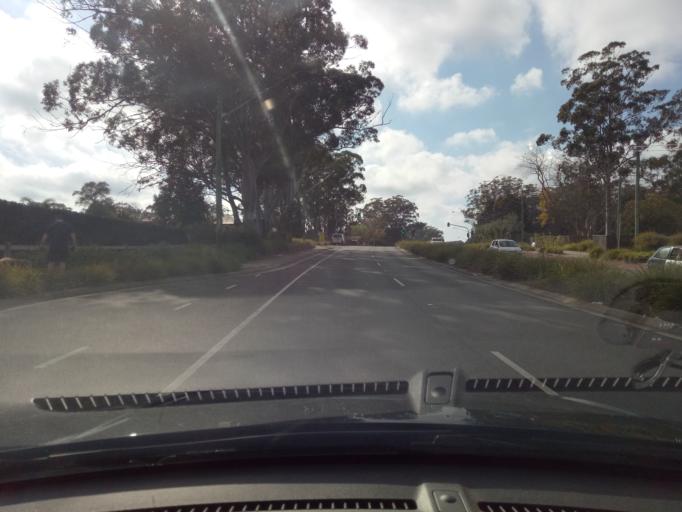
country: AU
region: New South Wales
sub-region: Gosford Shire
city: Erina
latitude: -33.4250
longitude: 151.4039
